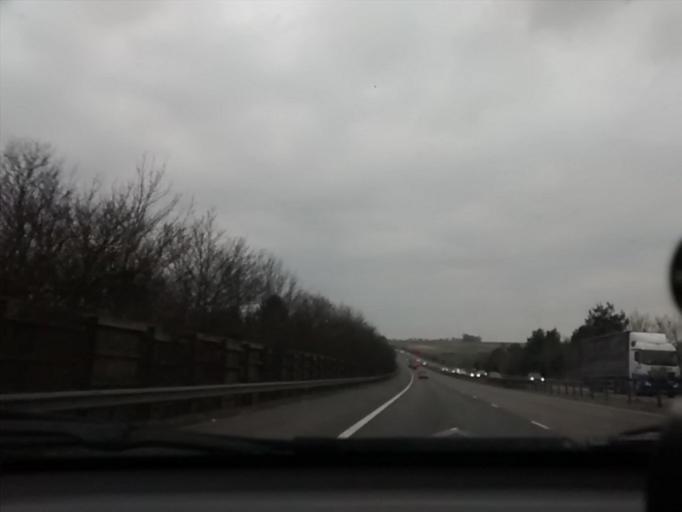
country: GB
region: England
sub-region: Essex
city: Saffron Walden
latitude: 52.0061
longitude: 0.1959
